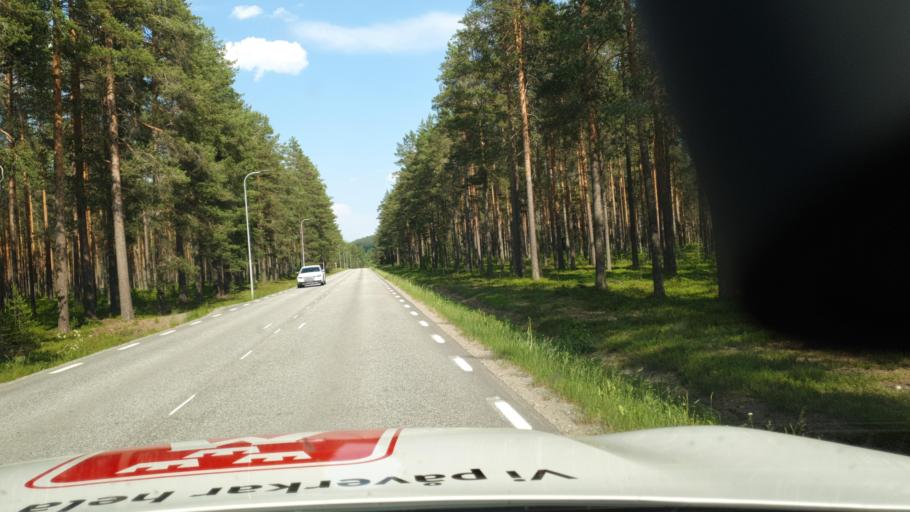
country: SE
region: Vaesterbotten
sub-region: Skelleftea Kommun
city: Forsbacka
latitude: 64.7208
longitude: 20.6840
